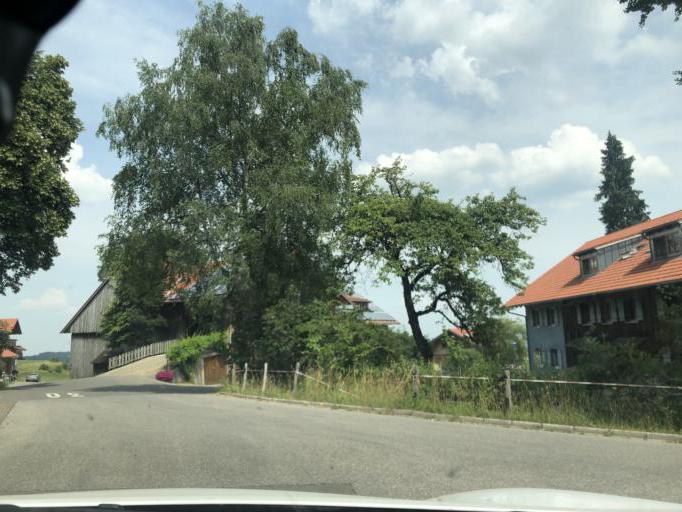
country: DE
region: Bavaria
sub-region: Swabia
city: Oy-Mittelberg
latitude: 47.6407
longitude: 10.4352
